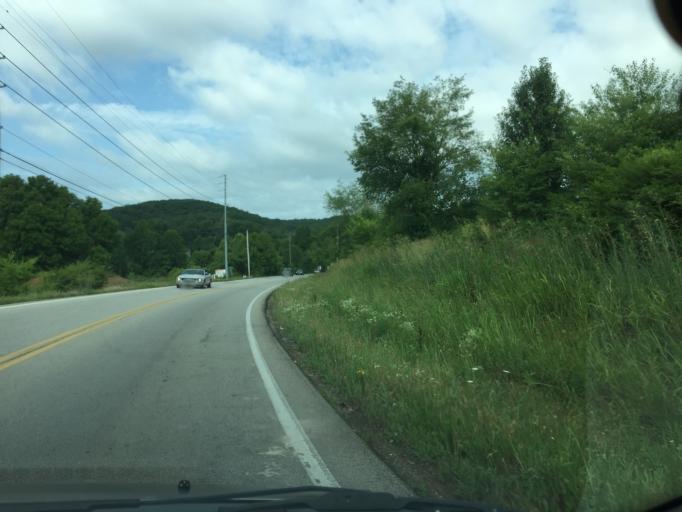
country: US
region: Tennessee
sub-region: Hamilton County
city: Apison
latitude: 34.9880
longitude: -85.0637
